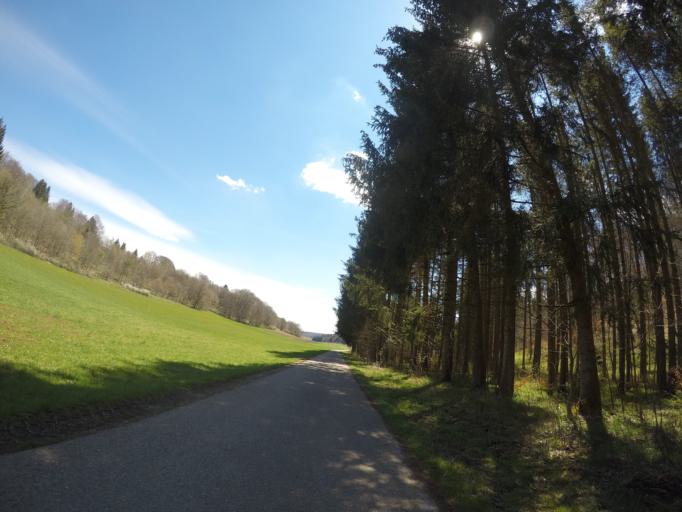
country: DE
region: Baden-Wuerttemberg
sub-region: Tuebingen Region
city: Westerheim
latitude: 48.5111
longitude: 9.6009
